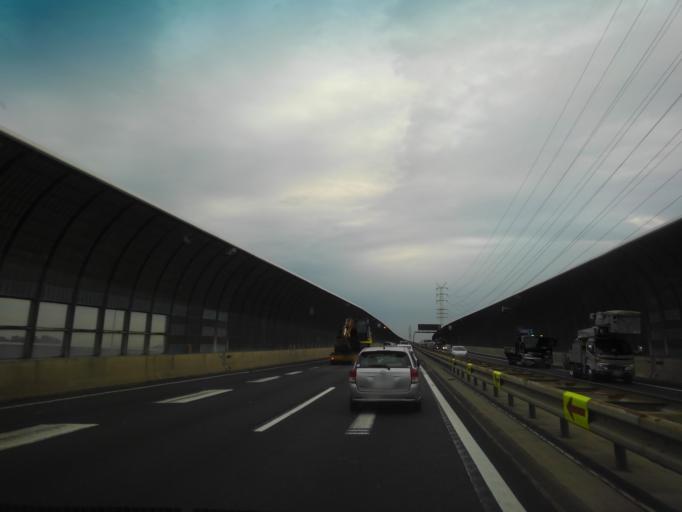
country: JP
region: Saitama
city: Shimotoda
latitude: 35.8395
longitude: 139.6792
